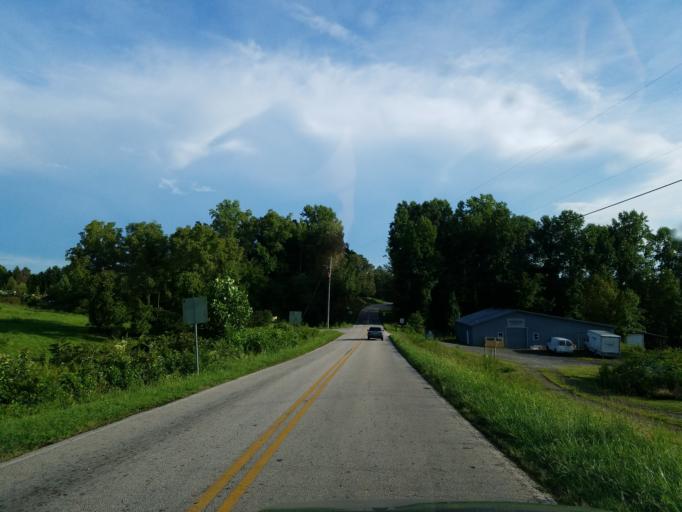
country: US
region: Georgia
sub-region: Lumpkin County
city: Dahlonega
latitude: 34.5606
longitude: -83.8851
